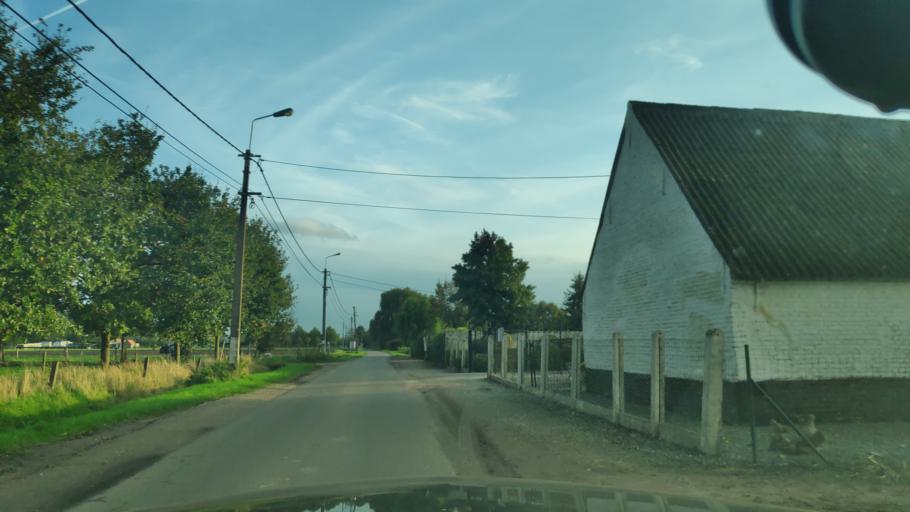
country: BE
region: Flanders
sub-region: Provincie Oost-Vlaanderen
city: Aalter
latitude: 51.1210
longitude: 3.4436
